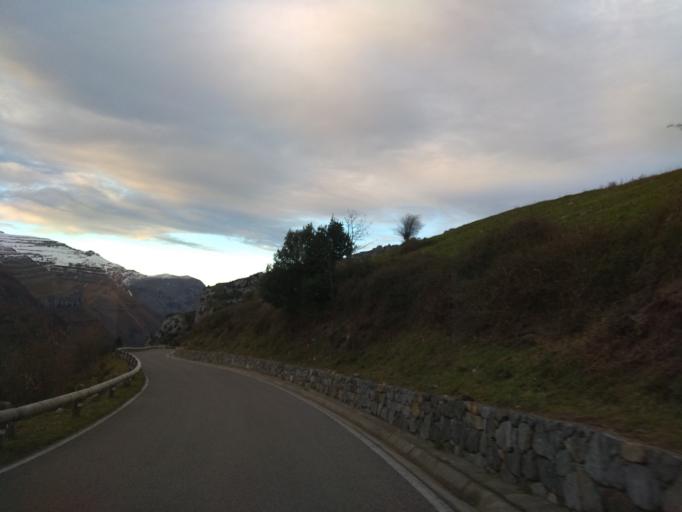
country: ES
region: Cantabria
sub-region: Provincia de Cantabria
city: Arredondo
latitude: 43.2036
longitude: -3.5819
